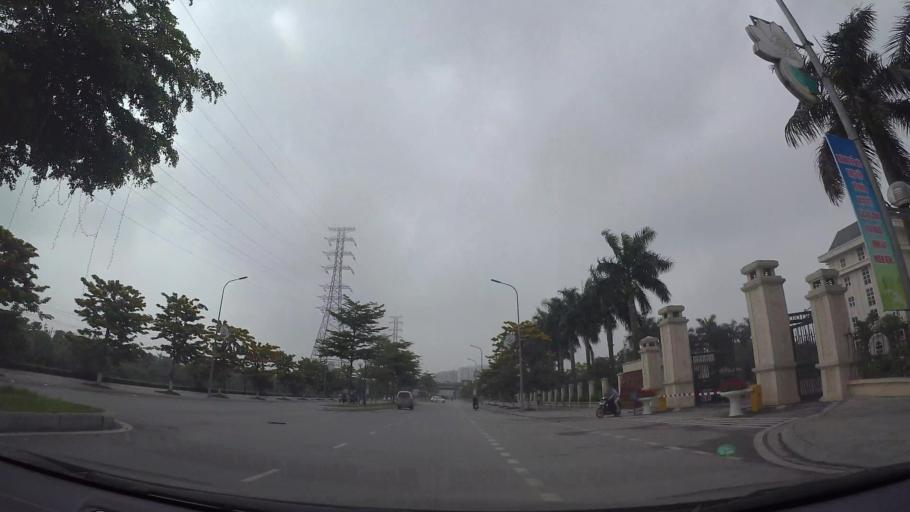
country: VN
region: Ha Noi
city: Van Dien
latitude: 20.9682
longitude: 105.8491
